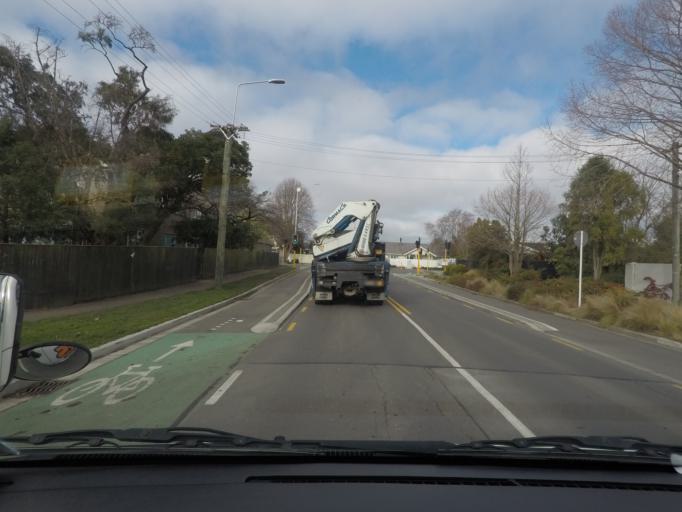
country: NZ
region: Canterbury
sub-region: Christchurch City
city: Christchurch
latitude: -43.5085
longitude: 172.6307
